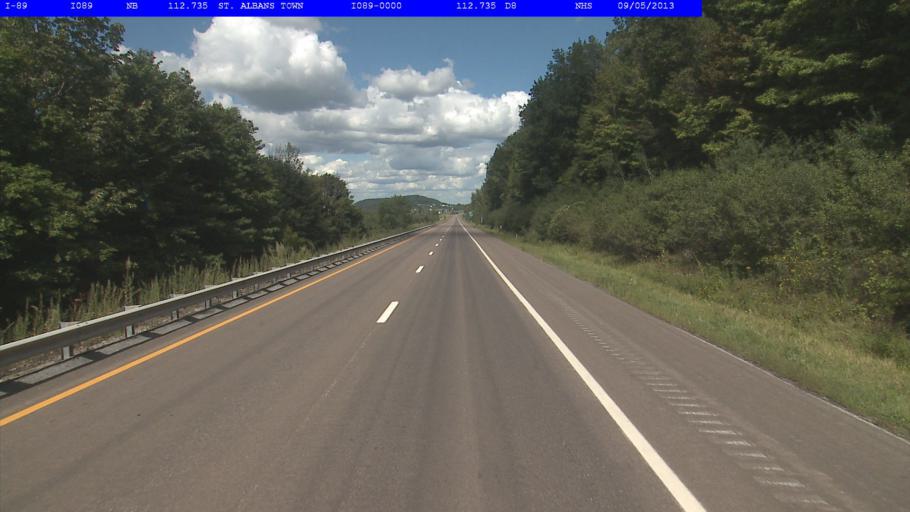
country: US
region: Vermont
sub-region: Franklin County
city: Saint Albans
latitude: 44.7805
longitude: -73.0732
